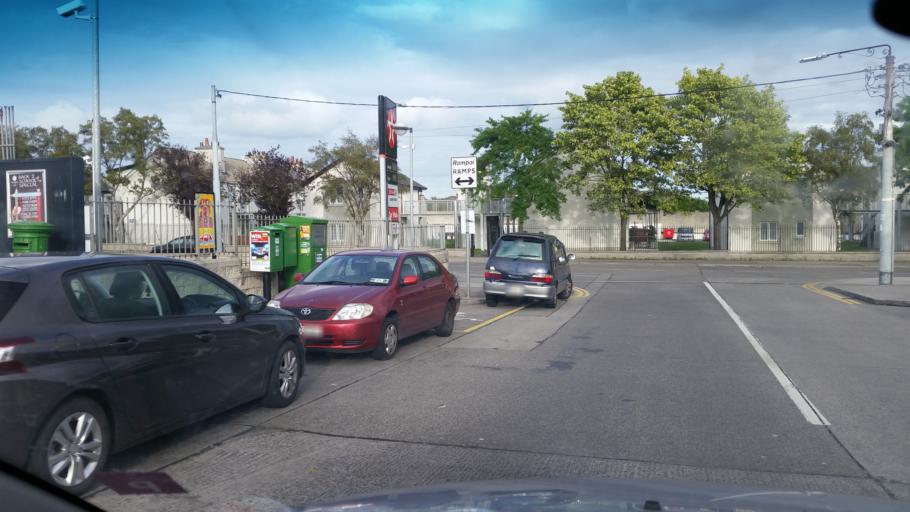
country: IE
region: Leinster
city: Glasnevin
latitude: 53.3826
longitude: -6.2769
